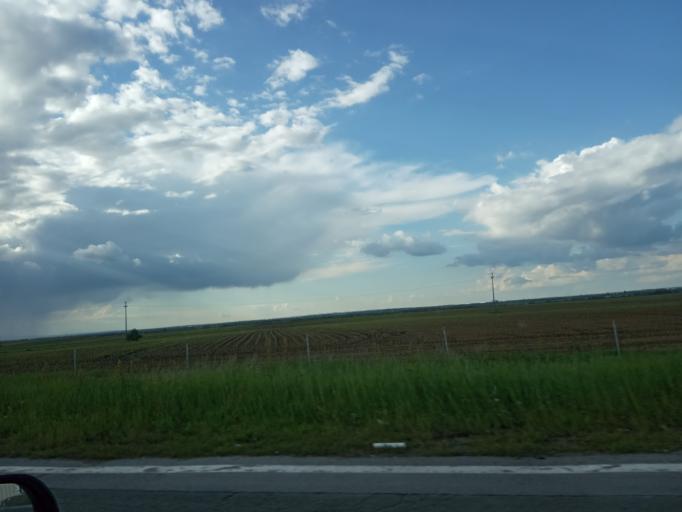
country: RS
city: Dobanovci
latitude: 44.8354
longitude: 20.2626
